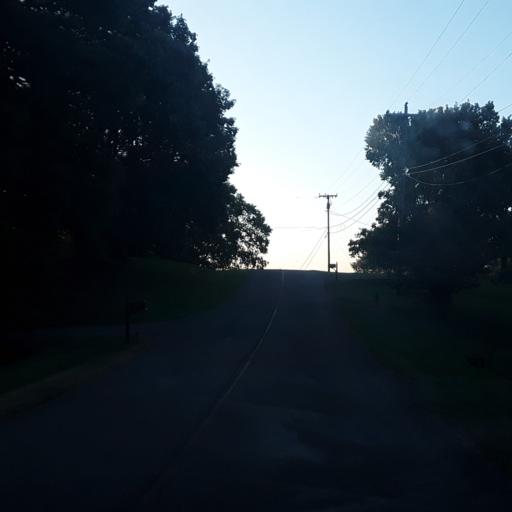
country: US
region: Tennessee
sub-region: Davidson County
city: Oak Hill
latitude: 36.0700
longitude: -86.7799
